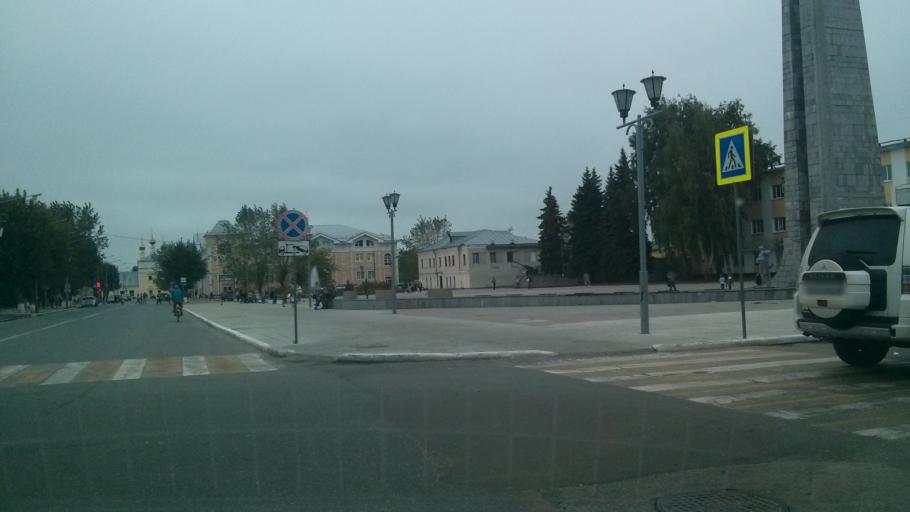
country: RU
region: Vladimir
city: Murom
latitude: 55.5757
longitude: 42.0502
